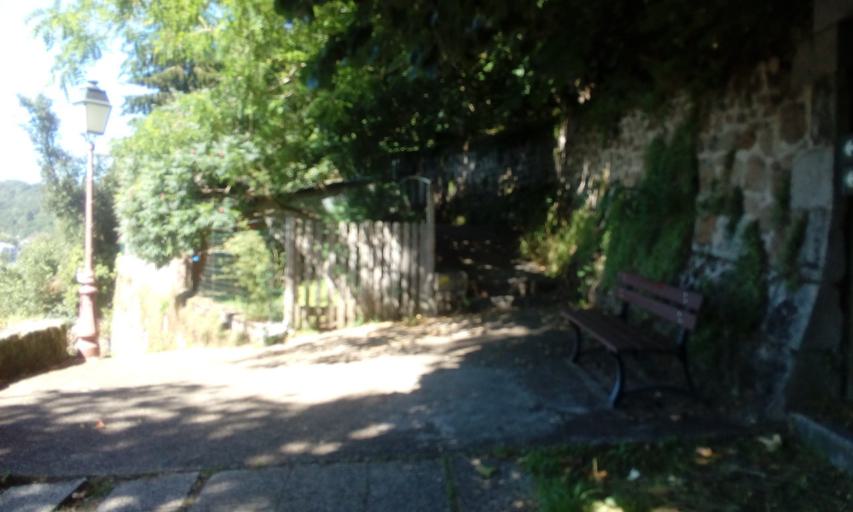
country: FR
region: Limousin
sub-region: Departement de la Creuse
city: Aubusson
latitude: 45.9575
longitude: 2.1702
